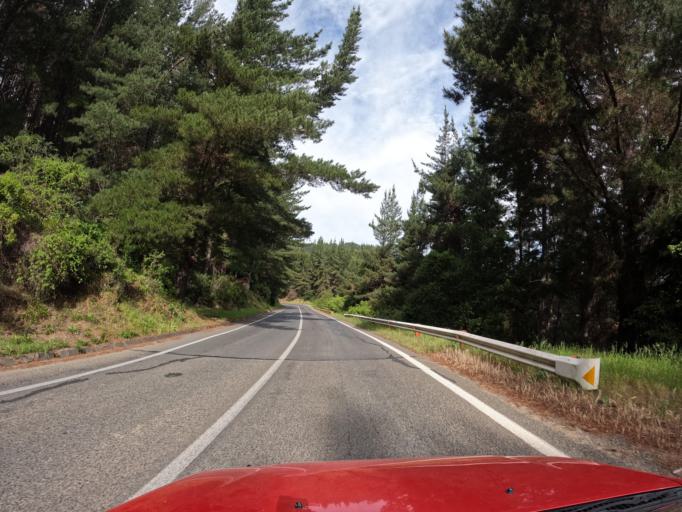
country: CL
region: Maule
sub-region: Provincia de Talca
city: Talca
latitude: -35.2971
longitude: -71.9695
